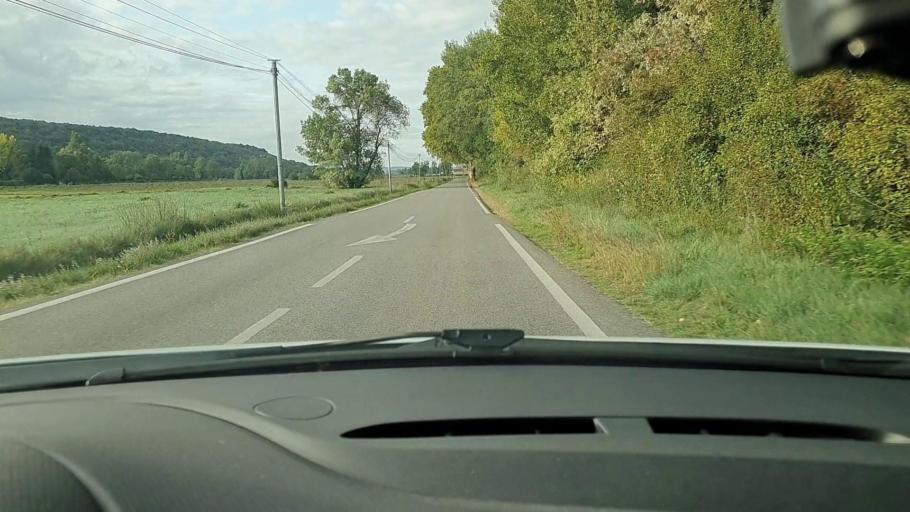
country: FR
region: Languedoc-Roussillon
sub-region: Departement du Gard
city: Saint-Ambroix
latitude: 44.1969
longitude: 4.2433
